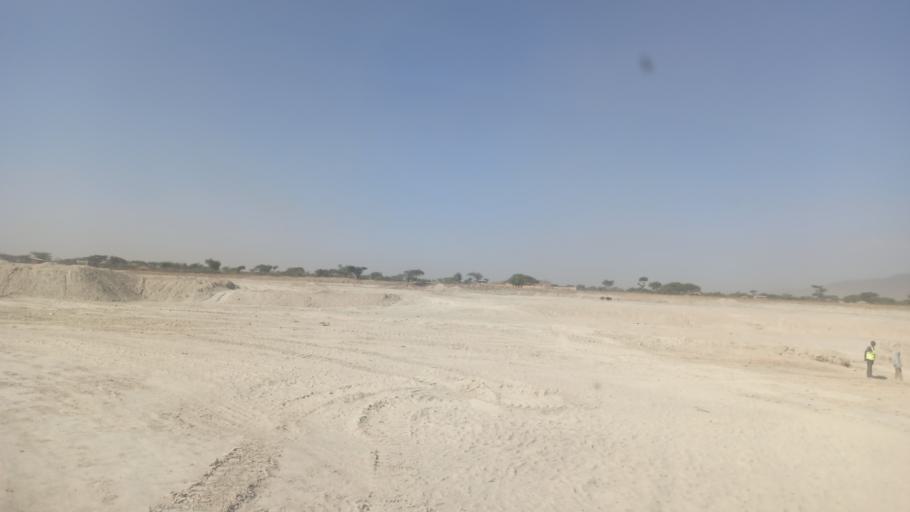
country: ET
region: Oromiya
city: Ziway
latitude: 7.6909
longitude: 38.6638
